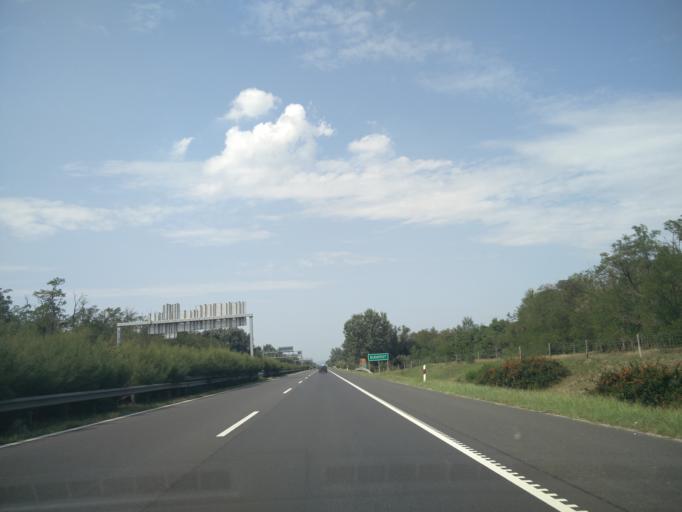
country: HU
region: Pest
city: Gyal
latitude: 47.3692
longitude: 19.1892
